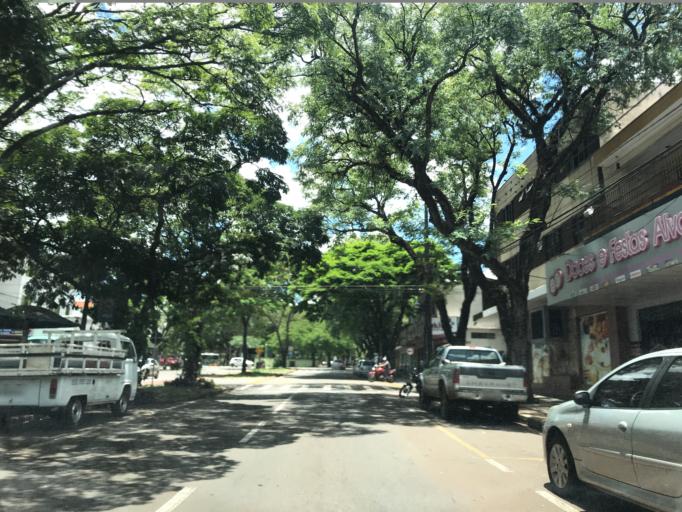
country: BR
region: Parana
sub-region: Maringa
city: Maringa
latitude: -23.4001
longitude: -51.9201
